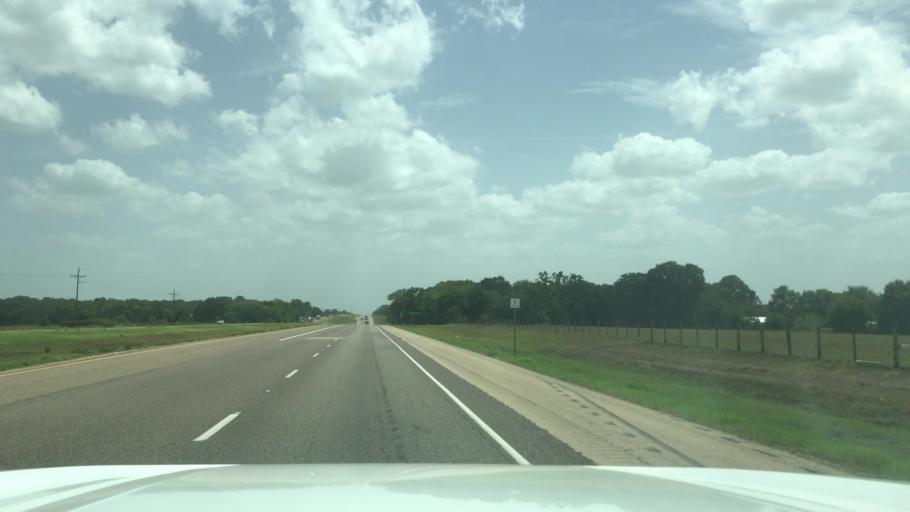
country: US
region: Texas
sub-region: Robertson County
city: Calvert
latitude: 31.0706
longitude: -96.7128
